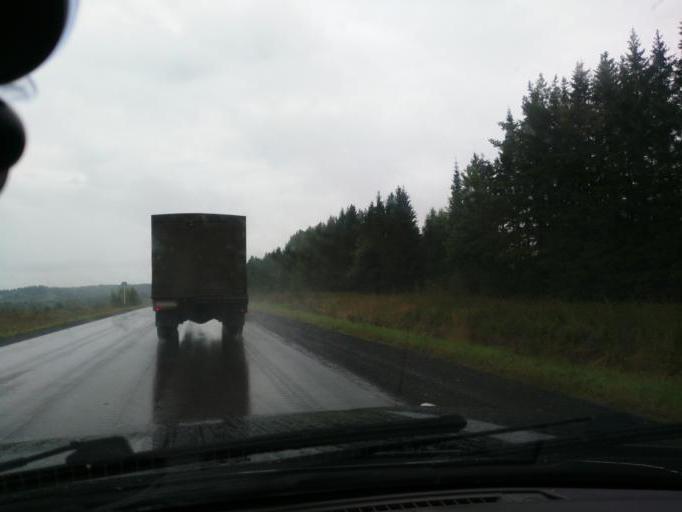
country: RU
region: Perm
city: Yugo-Kamskiy
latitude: 57.4719
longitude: 55.6770
